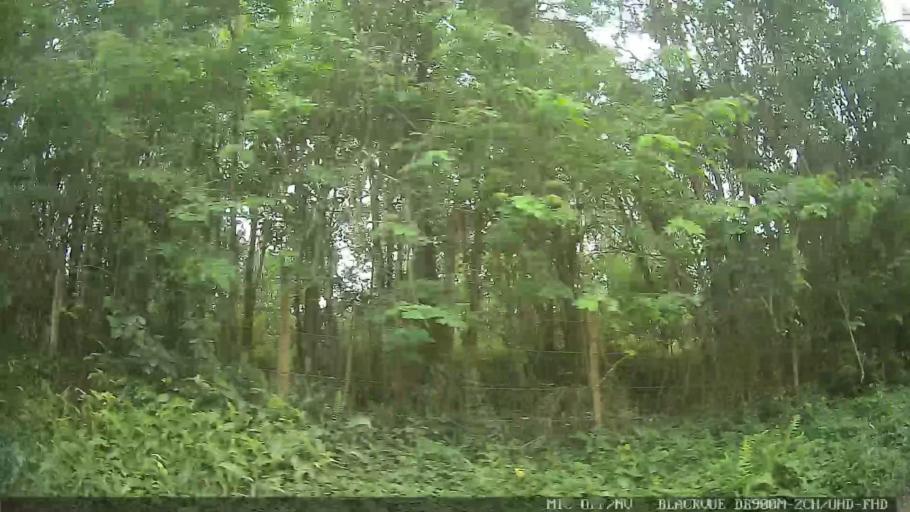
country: BR
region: Sao Paulo
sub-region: Suzano
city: Suzano
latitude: -23.5300
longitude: -46.2571
